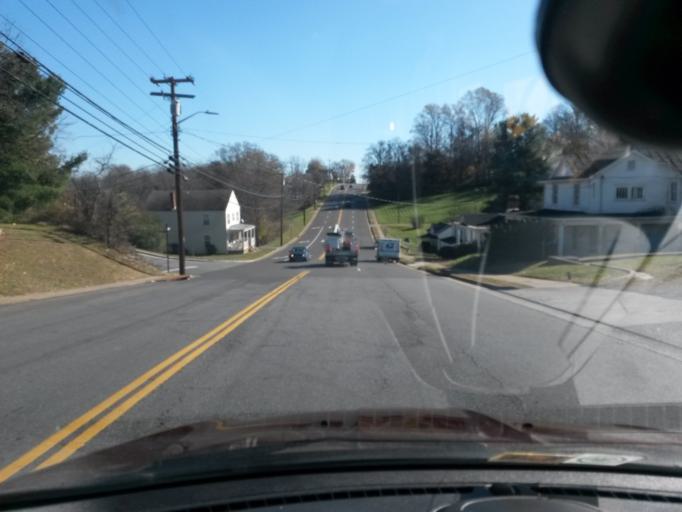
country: US
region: Virginia
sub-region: City of Bedford
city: Bedford
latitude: 37.3330
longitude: -79.5184
